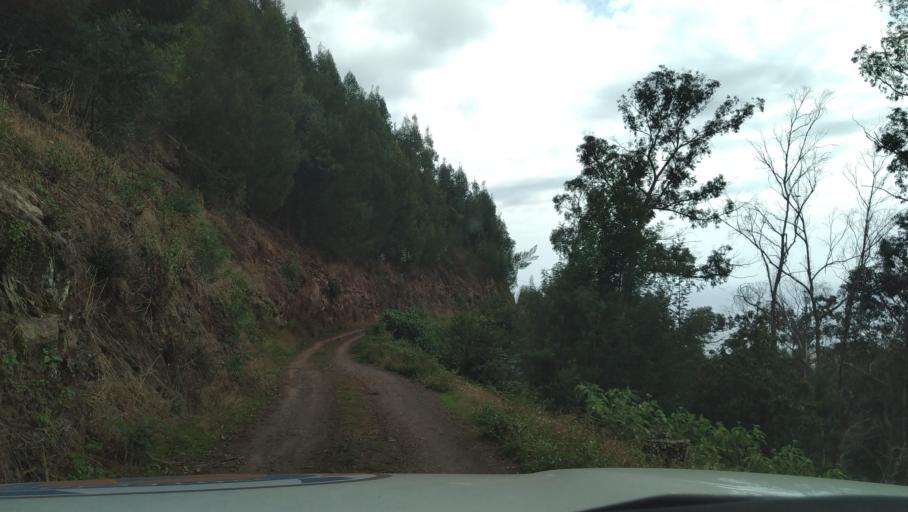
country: PT
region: Madeira
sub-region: Funchal
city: Nossa Senhora do Monte
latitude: 32.6822
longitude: -16.9240
